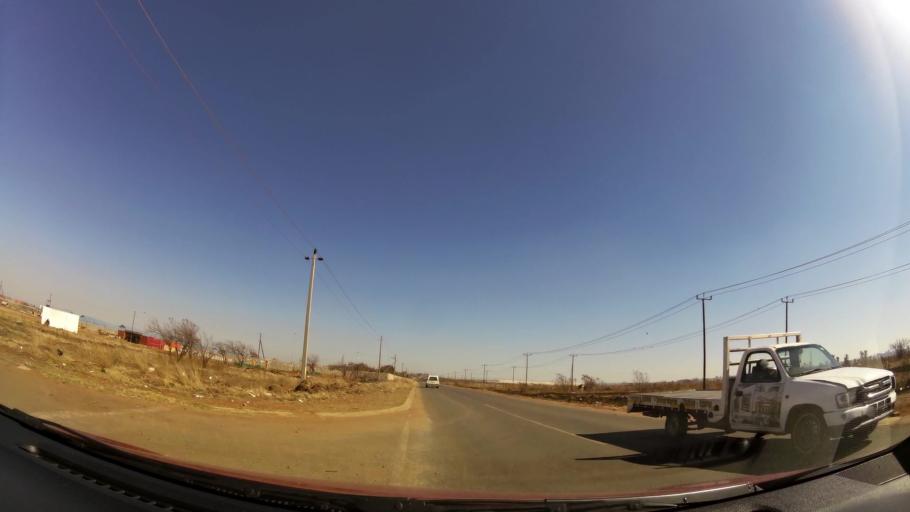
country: ZA
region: Gauteng
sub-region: City of Johannesburg Metropolitan Municipality
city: Soweto
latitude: -26.2155
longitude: 27.8295
